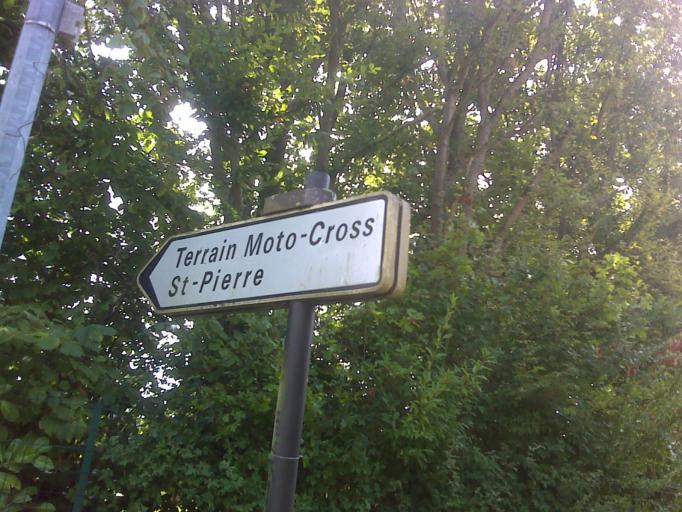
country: FR
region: Nord-Pas-de-Calais
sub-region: Departement du Nord
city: Conde-sur-l'Escaut
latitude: 50.4455
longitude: 3.5944
